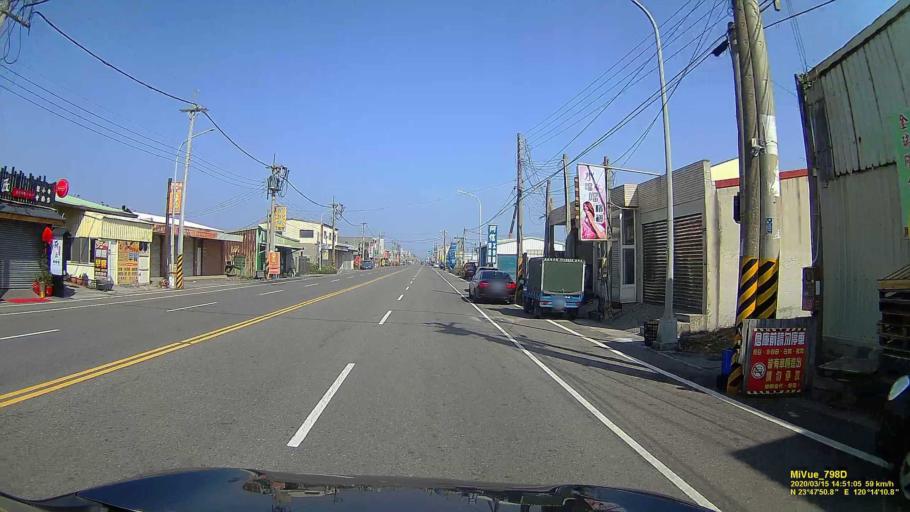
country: TW
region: Taiwan
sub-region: Yunlin
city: Douliu
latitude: 23.7974
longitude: 120.2366
